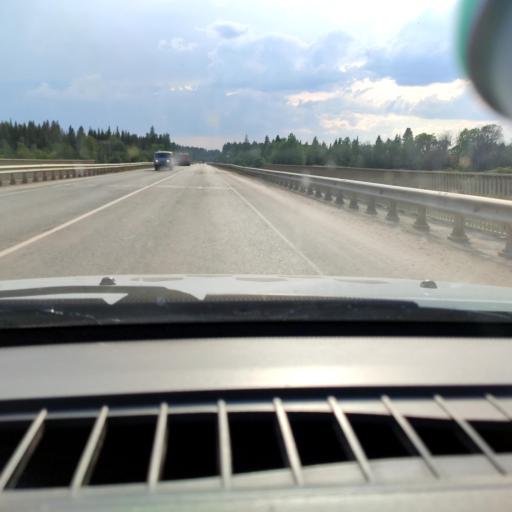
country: RU
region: Udmurtiya
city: Debesy
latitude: 57.6345
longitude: 53.7991
